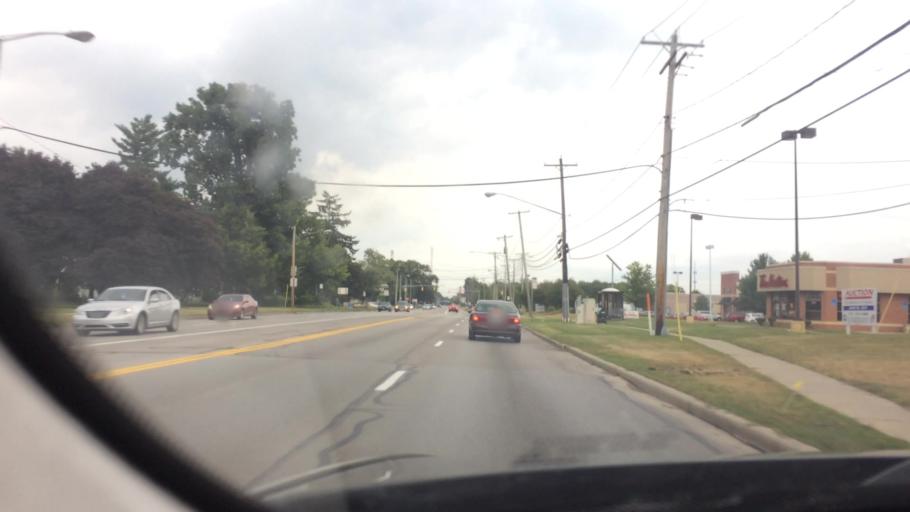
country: US
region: Ohio
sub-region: Wood County
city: Rossford
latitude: 41.6123
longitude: -83.6175
